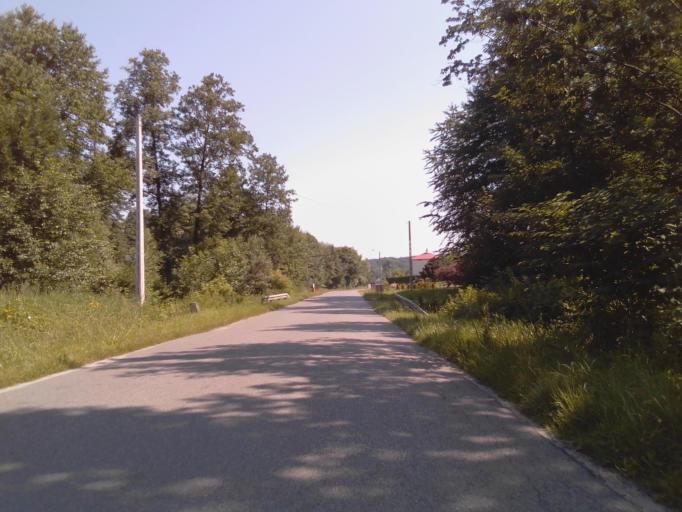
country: PL
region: Subcarpathian Voivodeship
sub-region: Powiat ropczycko-sedziszowski
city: Zagorzyce
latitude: 50.0326
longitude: 21.6501
